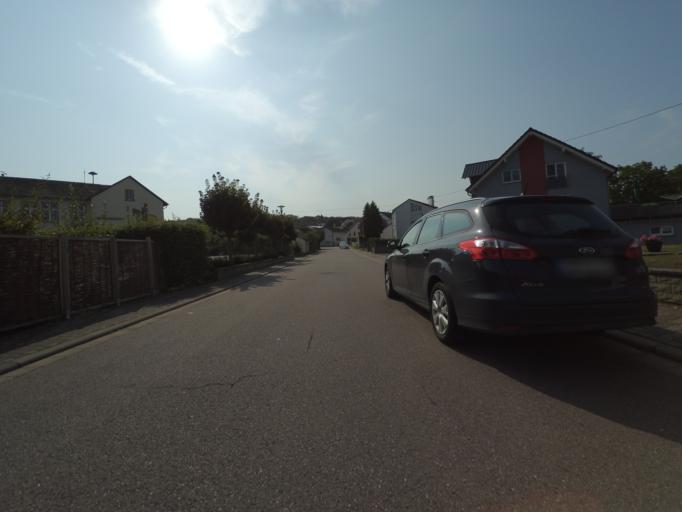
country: LU
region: Grevenmacher
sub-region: Canton de Remich
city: Remich
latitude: 49.5315
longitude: 6.3823
